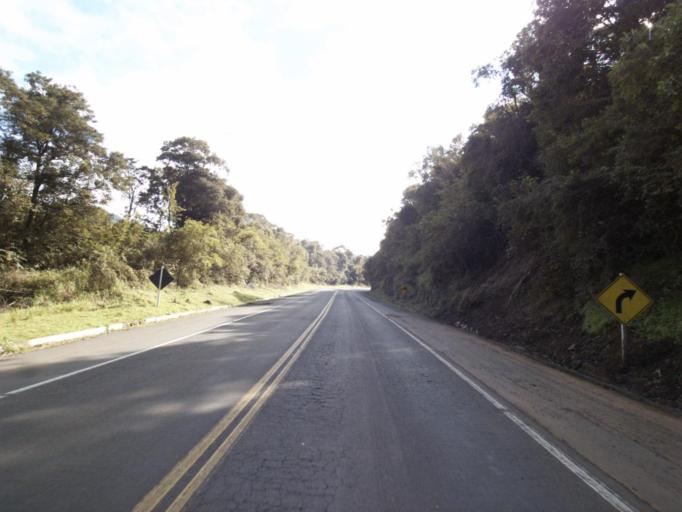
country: BR
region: Rio Grande do Sul
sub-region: Frederico Westphalen
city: Frederico Westphalen
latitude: -27.1556
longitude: -53.2166
